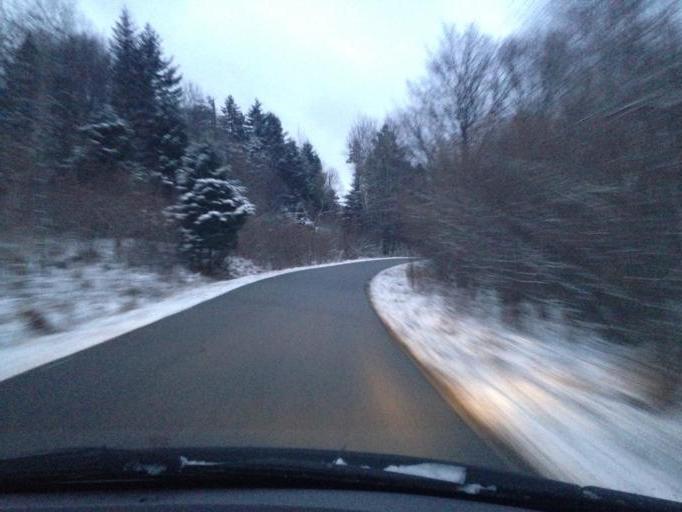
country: PL
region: Subcarpathian Voivodeship
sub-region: Powiat jasielski
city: Krempna
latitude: 49.5108
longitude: 21.5413
